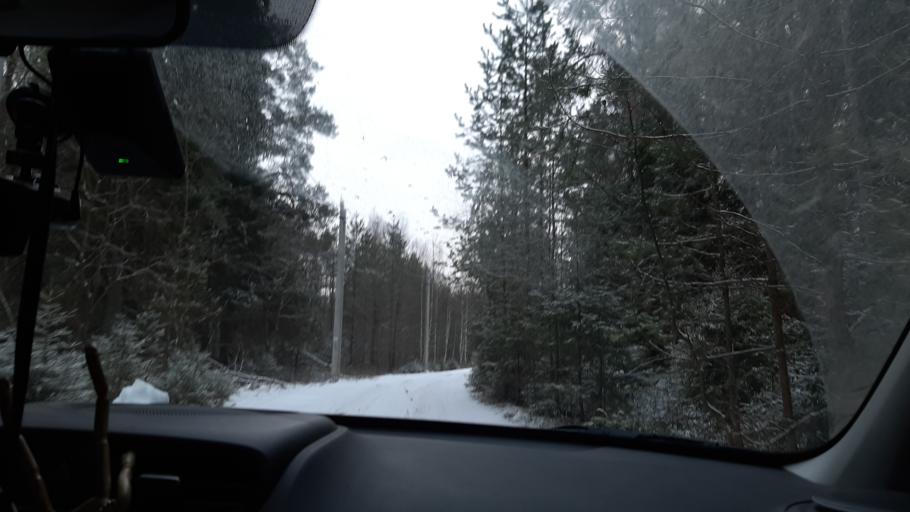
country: RU
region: Ivanovo
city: Kokhma
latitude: 56.8986
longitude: 41.0107
